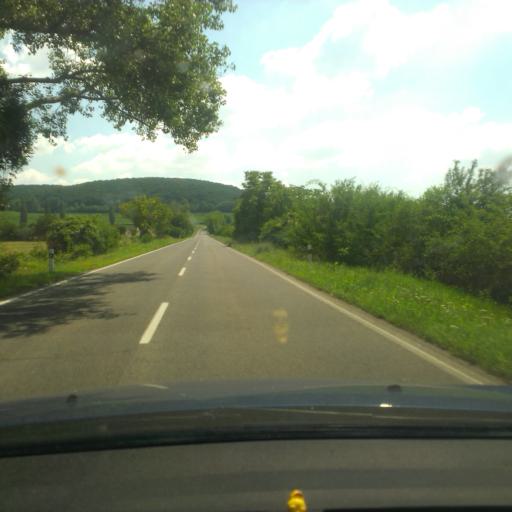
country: SK
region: Trnavsky
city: Hlohovec
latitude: 48.4658
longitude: 17.8134
